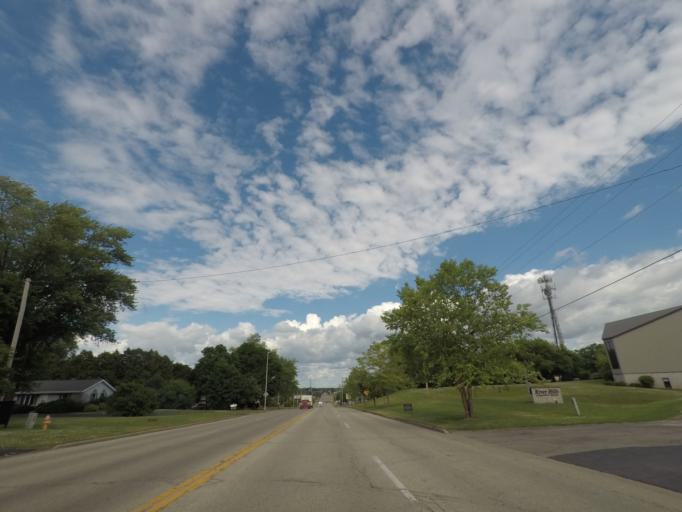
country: US
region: Wisconsin
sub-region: Rock County
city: Janesville
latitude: 42.6791
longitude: -89.0580
